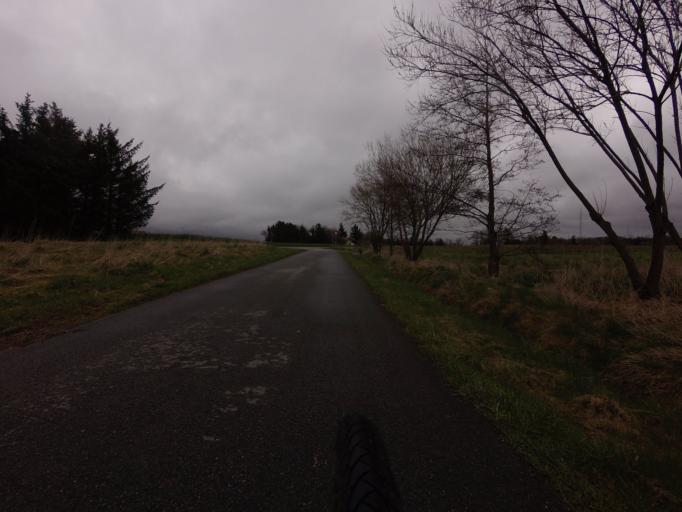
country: DK
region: North Denmark
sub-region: Jammerbugt Kommune
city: Pandrup
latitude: 57.3373
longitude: 9.7809
